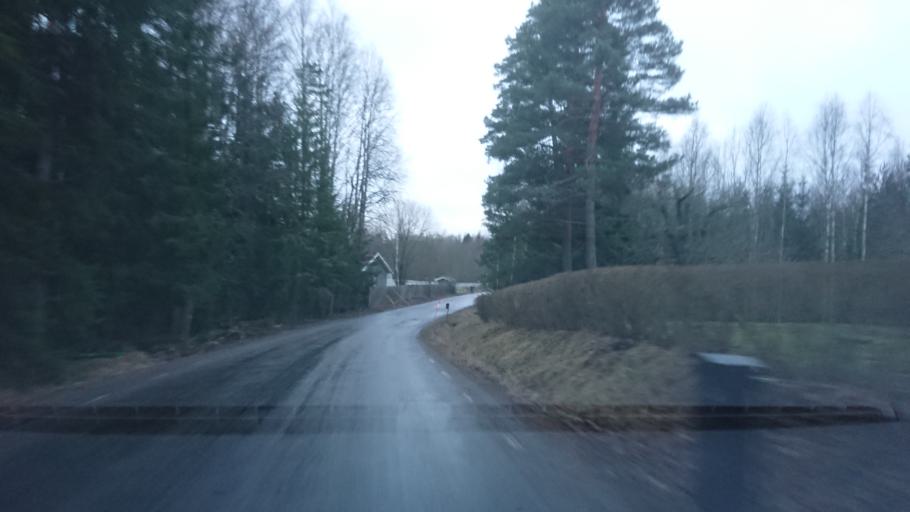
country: SE
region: Uppsala
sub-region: Osthammars Kommun
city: Bjorklinge
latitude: 59.9955
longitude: 17.5941
